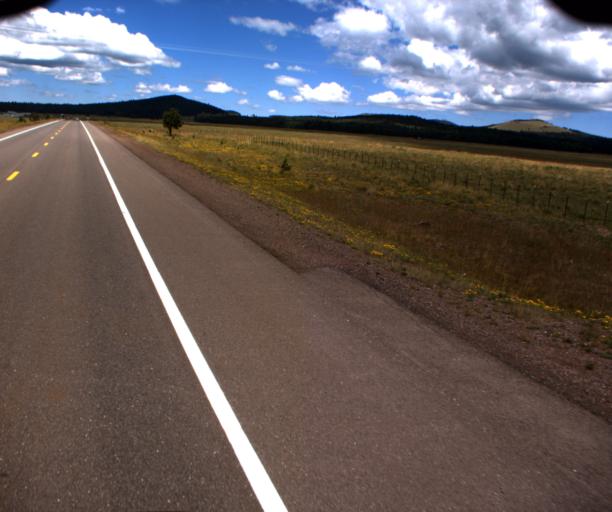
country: US
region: Arizona
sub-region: Apache County
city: Eagar
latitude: 34.0316
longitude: -109.5849
